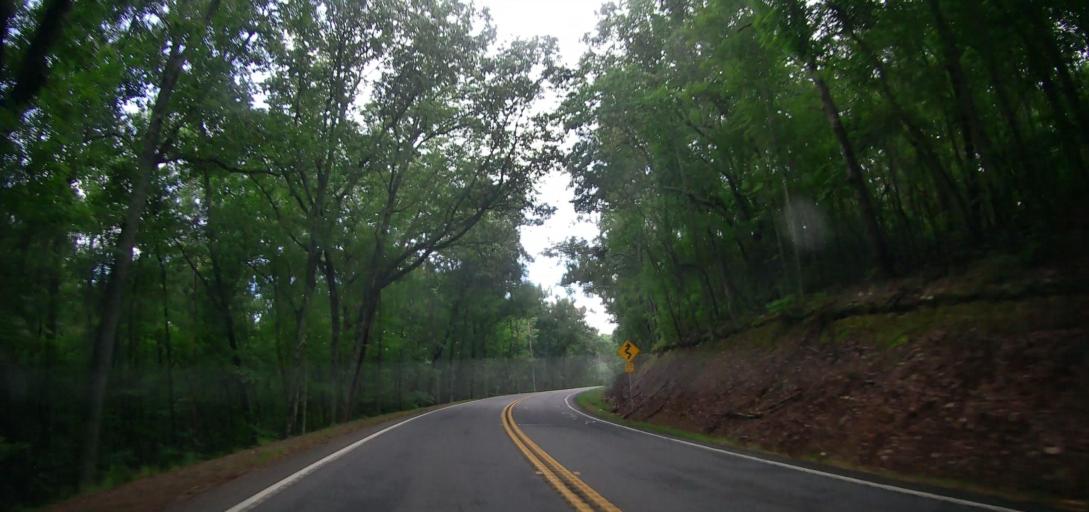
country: US
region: Georgia
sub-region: Harris County
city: Pine Mountain
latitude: 32.8457
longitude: -84.8101
